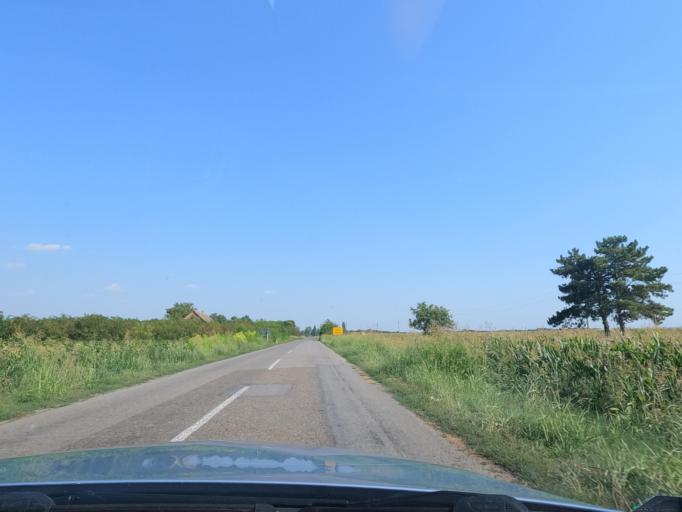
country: RS
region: Autonomna Pokrajina Vojvodina
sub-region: Juznobacki Okrug
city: Becej
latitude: 45.6367
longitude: 20.0049
